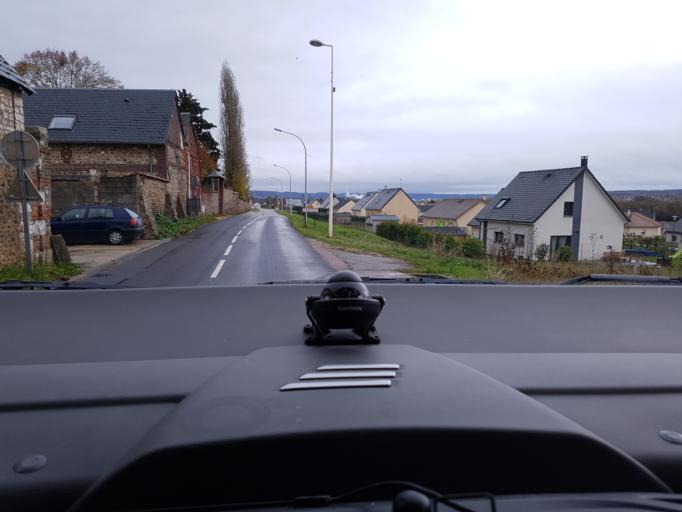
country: FR
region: Haute-Normandie
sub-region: Departement de l'Eure
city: Igoville
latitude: 49.3205
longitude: 1.1343
